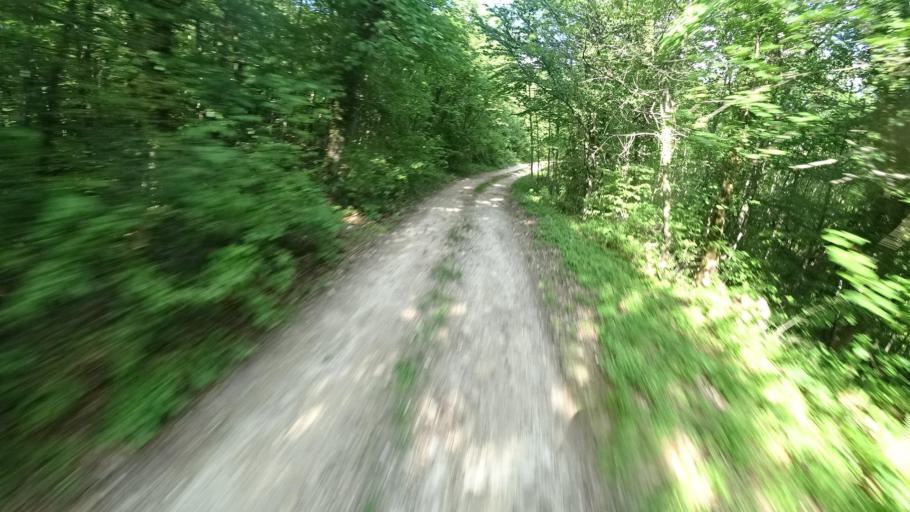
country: BA
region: Federation of Bosnia and Herzegovina
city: Sanica
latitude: 44.6544
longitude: 16.6076
